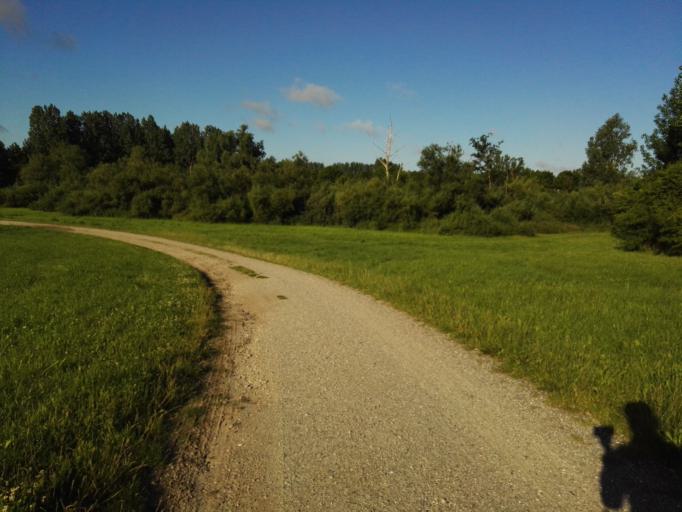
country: DK
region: Capital Region
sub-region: Ballerup Kommune
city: Ballerup
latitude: 55.7184
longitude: 12.3778
